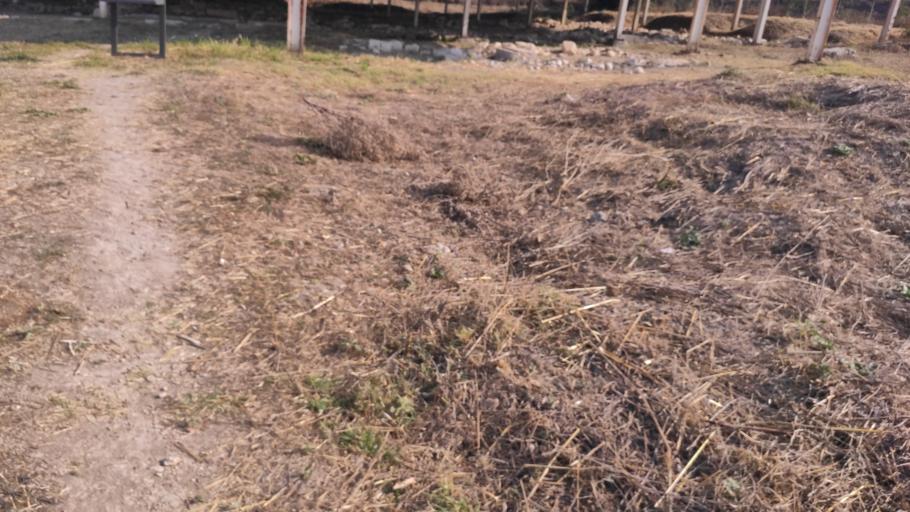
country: GR
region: Central Macedonia
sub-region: Nomos Pellis
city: Pella
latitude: 40.7573
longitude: 22.5191
